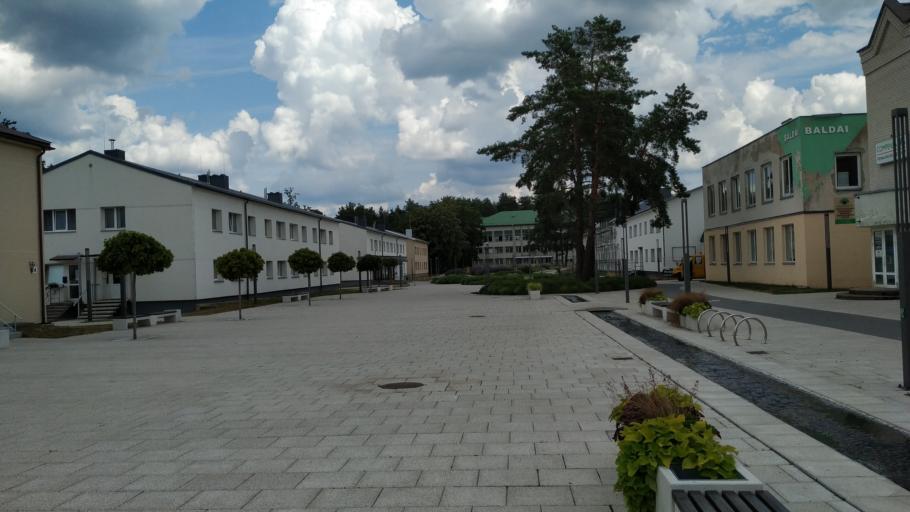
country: LT
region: Alytaus apskritis
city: Varena
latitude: 54.2113
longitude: 24.5716
